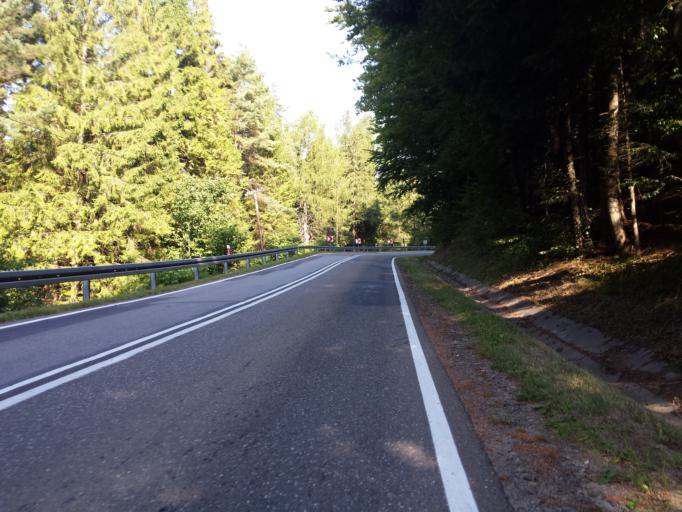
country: PL
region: Subcarpathian Voivodeship
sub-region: Powiat leski
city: Cisna
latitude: 49.2388
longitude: 22.2996
